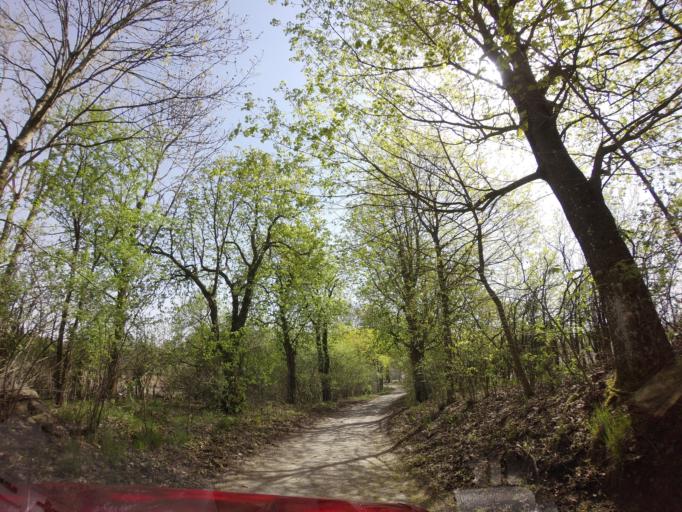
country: PL
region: West Pomeranian Voivodeship
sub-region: Powiat choszczenski
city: Recz
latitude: 53.2438
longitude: 15.6147
